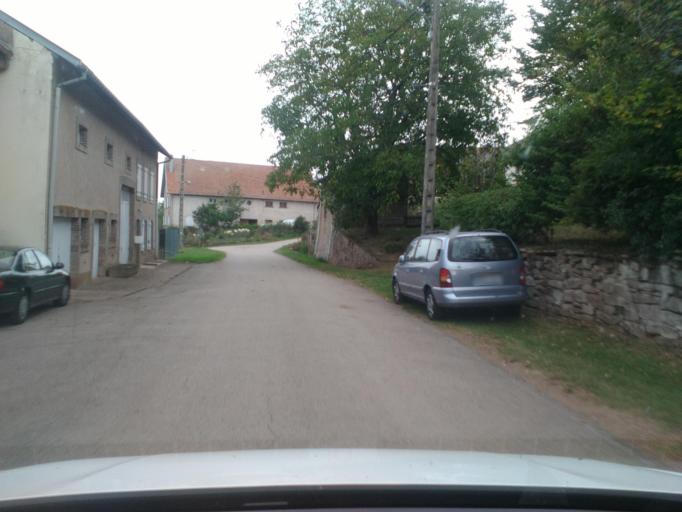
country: FR
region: Lorraine
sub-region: Departement des Vosges
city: Senones
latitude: 48.3483
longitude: 6.9942
